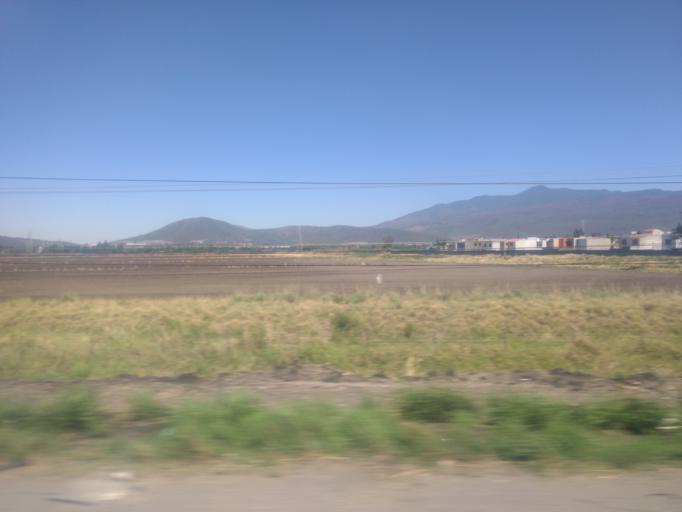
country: MX
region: Jalisco
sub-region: Tlajomulco de Zuniga
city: Santa Cruz de las Flores
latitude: 20.4637
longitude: -103.5104
